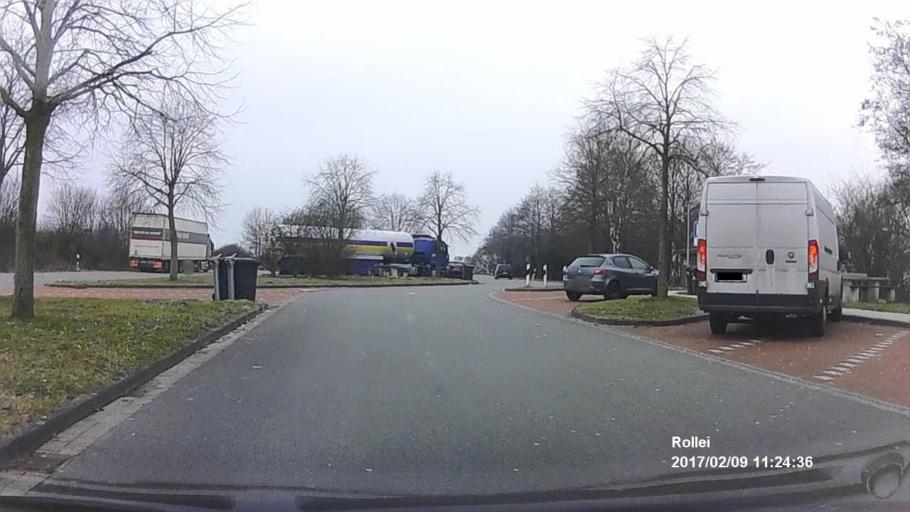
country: DE
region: Lower Saxony
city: Jemgum
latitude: 53.2227
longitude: 7.3718
